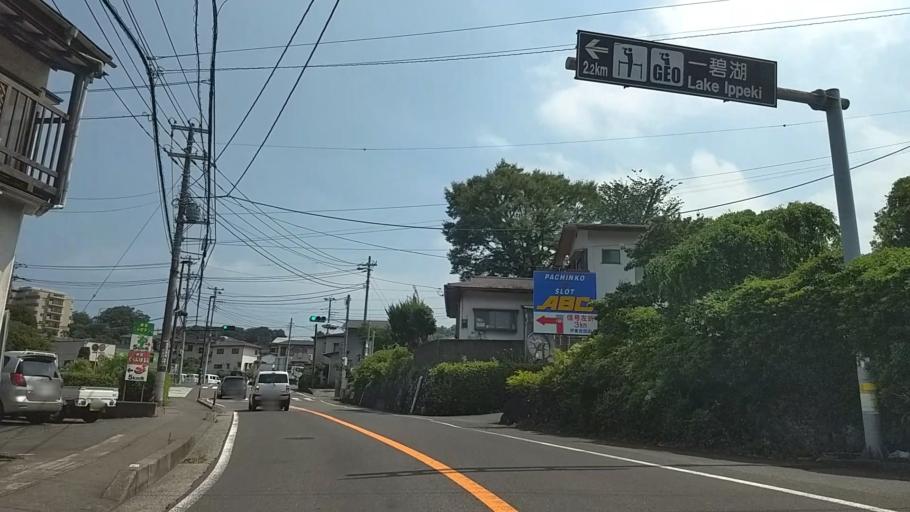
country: JP
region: Shizuoka
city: Ito
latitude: 34.9352
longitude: 139.0916
